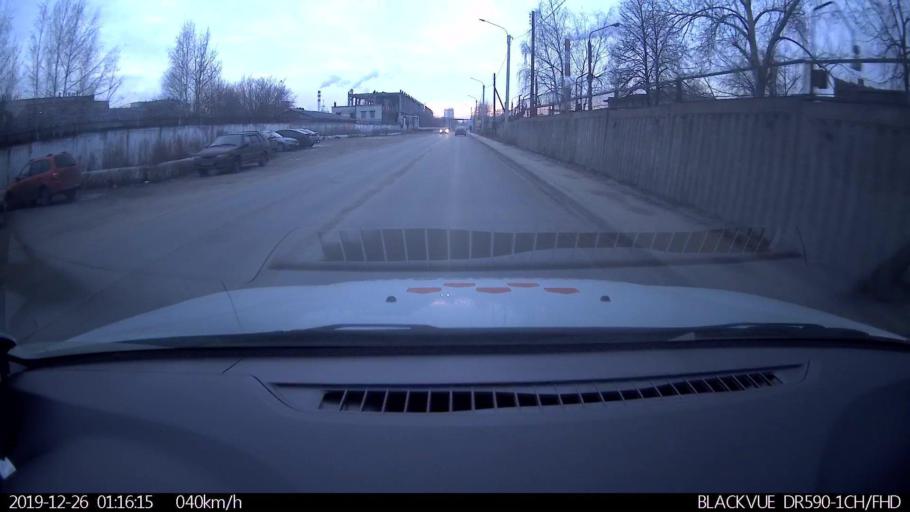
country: RU
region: Nizjnij Novgorod
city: Nizhniy Novgorod
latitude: 56.2707
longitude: 43.9093
